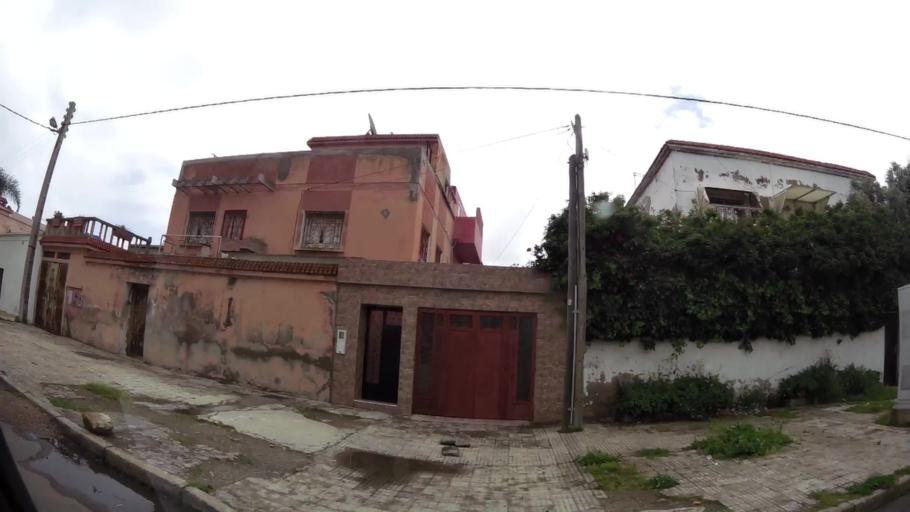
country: MA
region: Grand Casablanca
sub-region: Mediouna
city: Tit Mellil
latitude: 33.6132
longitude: -7.5249
